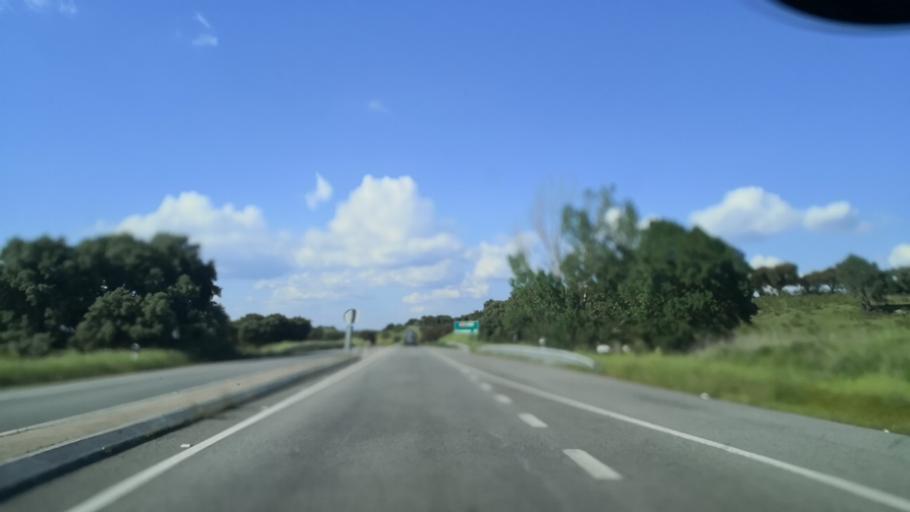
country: PT
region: Portalegre
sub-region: Arronches
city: Arronches
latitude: 39.0626
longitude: -7.4372
